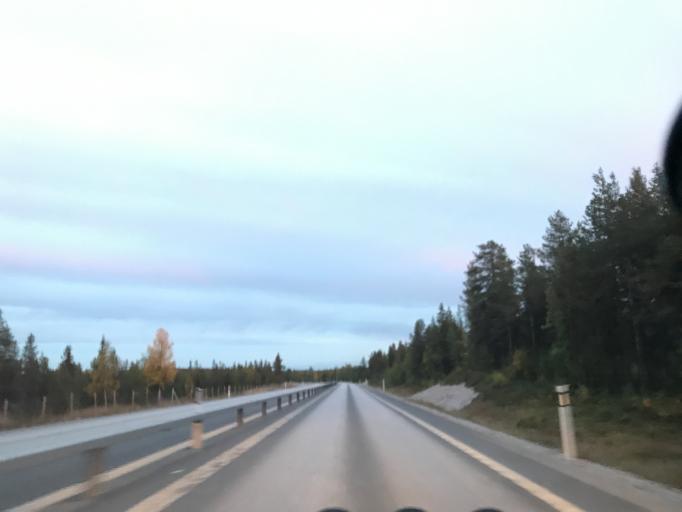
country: SE
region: Norrbotten
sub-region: Gallivare Kommun
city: Malmberget
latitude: 67.6629
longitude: 20.9936
